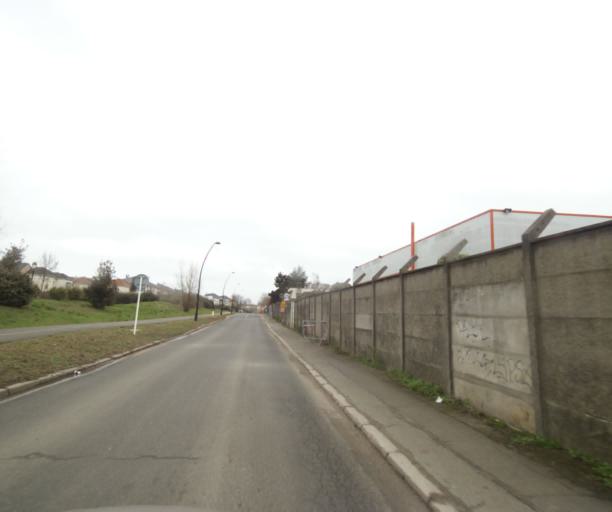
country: FR
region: Ile-de-France
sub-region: Departement du Val-de-Marne
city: Ablon-sur-Seine
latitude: 48.7419
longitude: 2.4302
